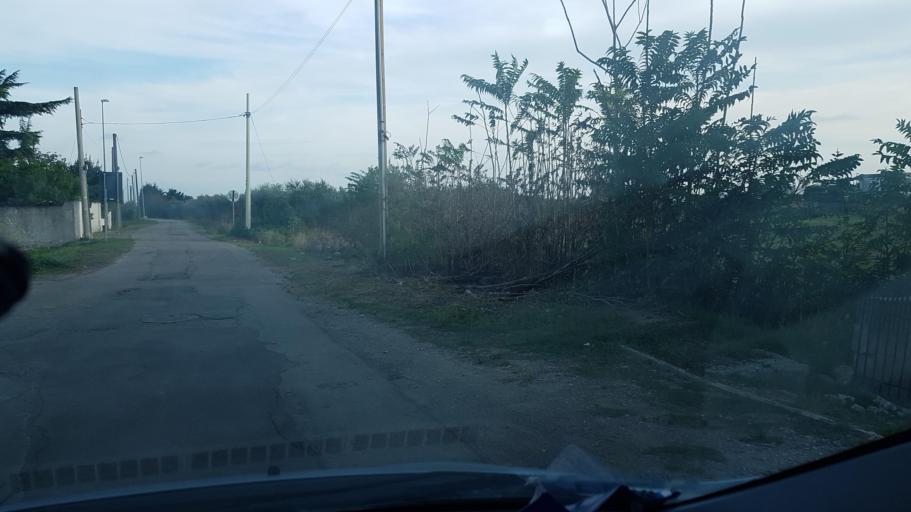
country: IT
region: Apulia
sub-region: Provincia di Lecce
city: Veglie
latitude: 40.3324
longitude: 17.9749
